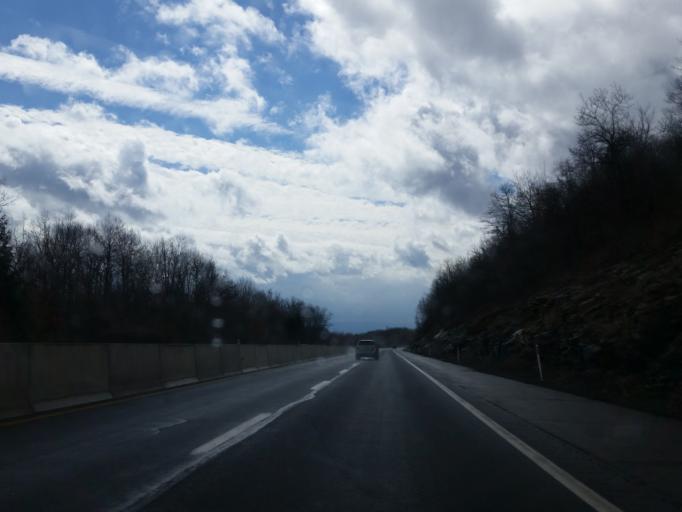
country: US
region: Pennsylvania
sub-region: Lackawanna County
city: Chinchilla
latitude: 41.4496
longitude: -75.6885
